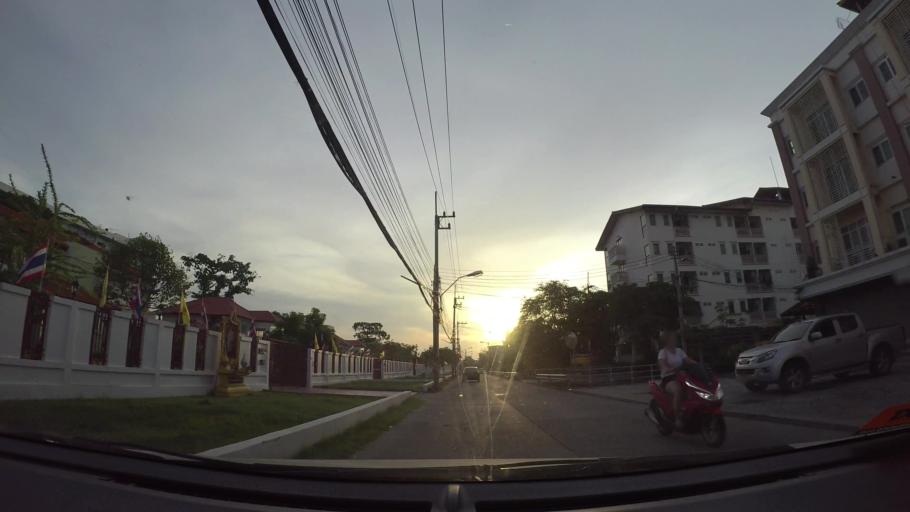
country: TH
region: Chon Buri
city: Chon Buri
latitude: 13.3560
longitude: 100.9817
